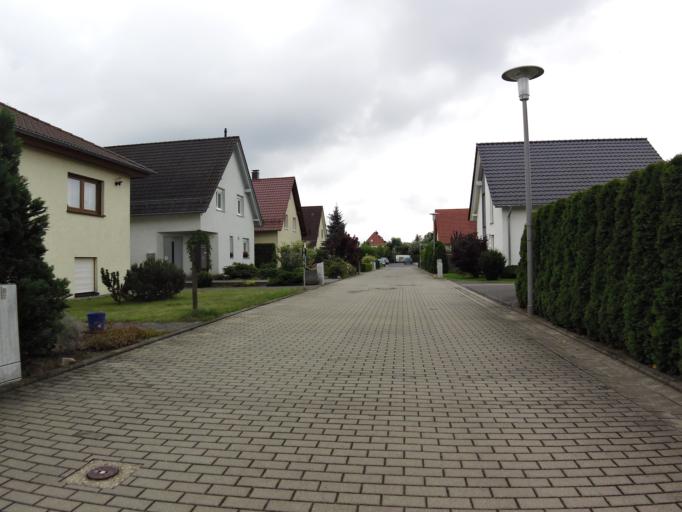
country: DE
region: Saxony
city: Taucha
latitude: 51.3513
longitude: 12.4868
